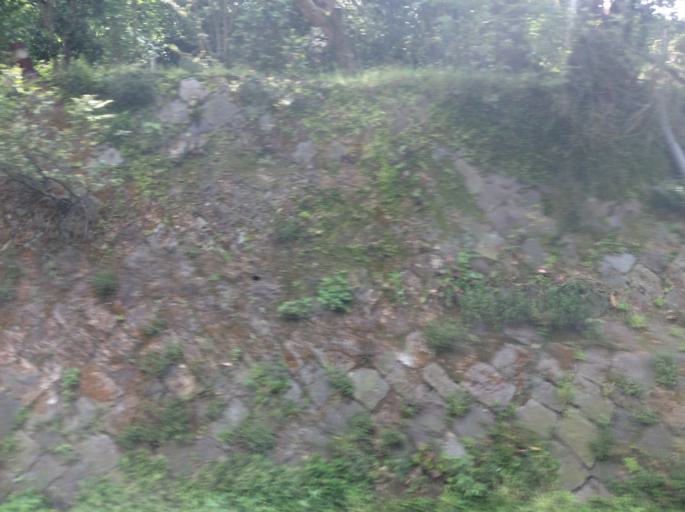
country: TW
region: Taipei
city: Taipei
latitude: 25.1640
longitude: 121.5444
